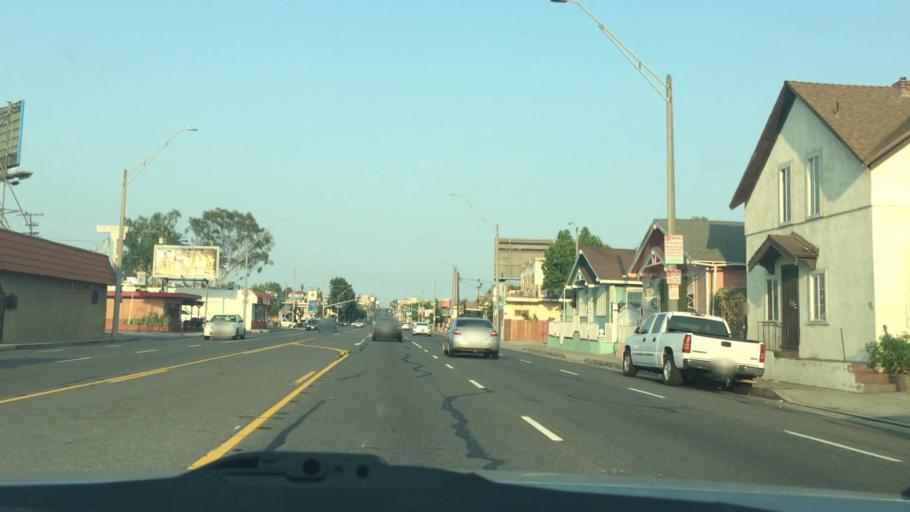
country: US
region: California
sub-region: Los Angeles County
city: Signal Hill
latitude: 33.7898
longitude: -118.1705
